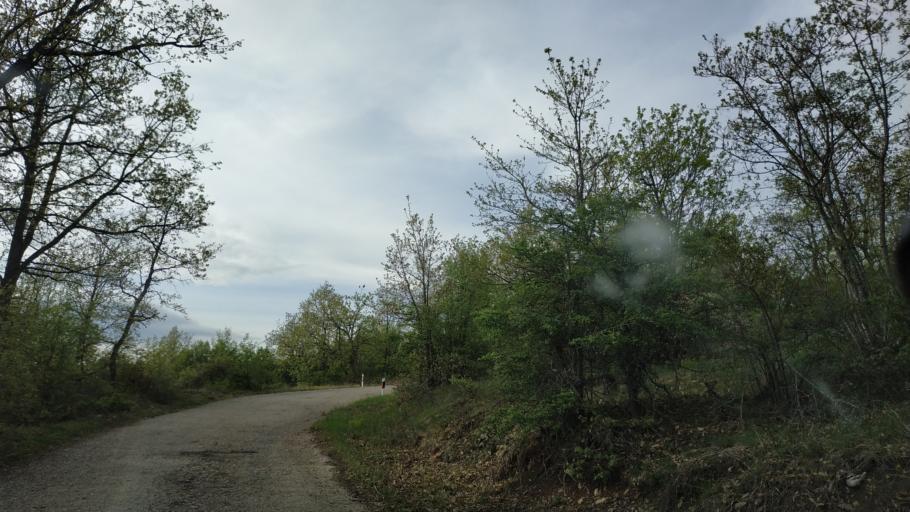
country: RS
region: Central Serbia
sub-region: Zajecarski Okrug
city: Soko Banja
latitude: 43.5417
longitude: 21.8785
